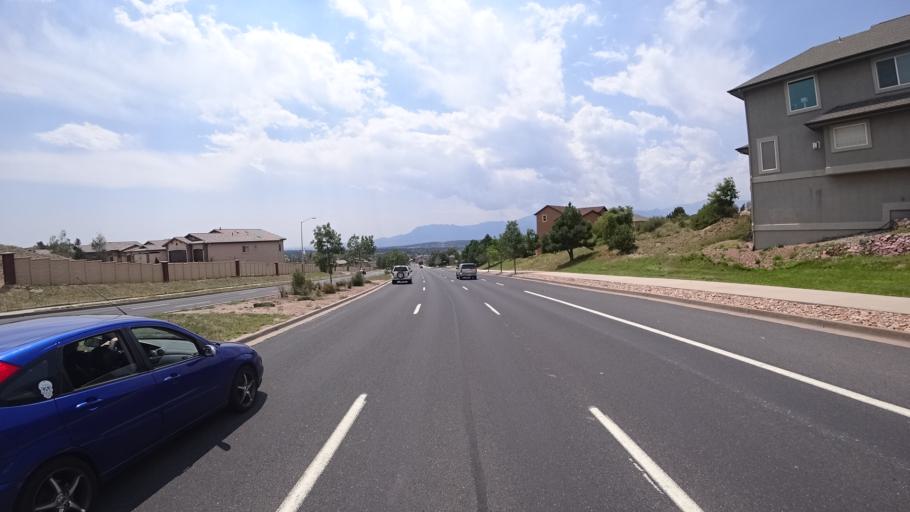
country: US
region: Colorado
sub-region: El Paso County
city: Cimarron Hills
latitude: 38.9123
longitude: -104.7344
